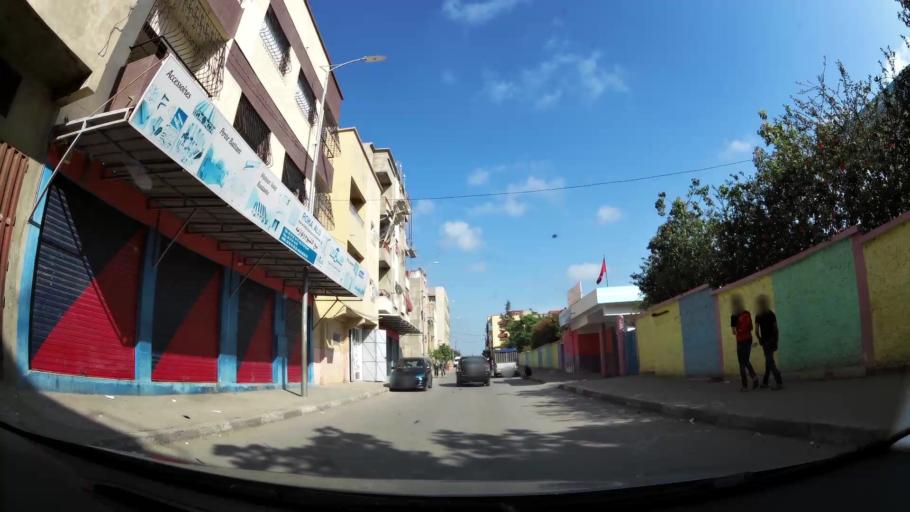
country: MA
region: Rabat-Sale-Zemmour-Zaer
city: Sale
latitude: 34.0618
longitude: -6.7712
